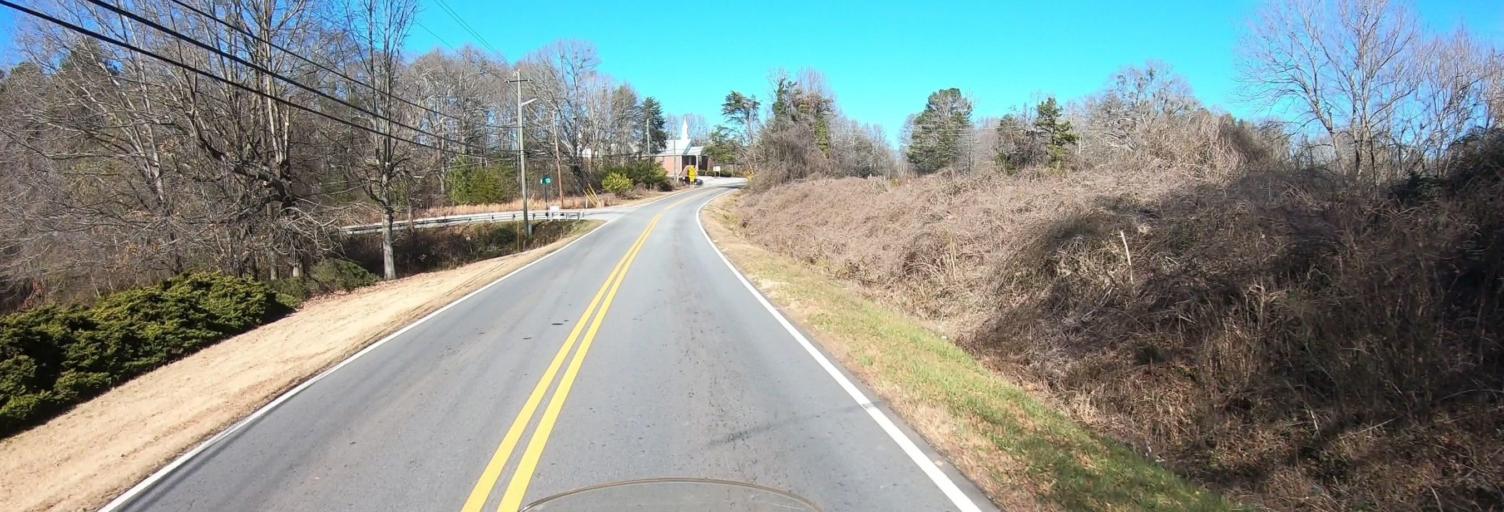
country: US
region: Georgia
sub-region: Hall County
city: Gainesville
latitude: 34.3214
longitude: -83.7938
